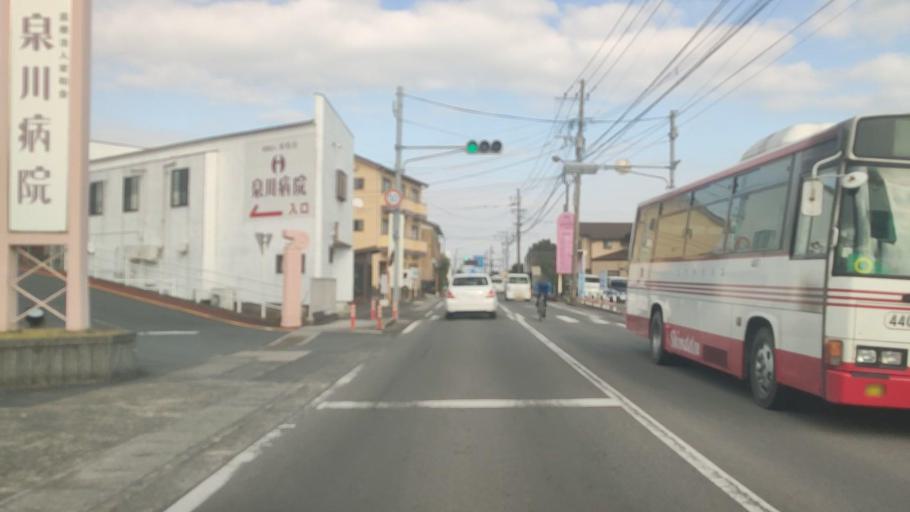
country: JP
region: Nagasaki
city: Shimabara
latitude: 32.7179
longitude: 130.3518
